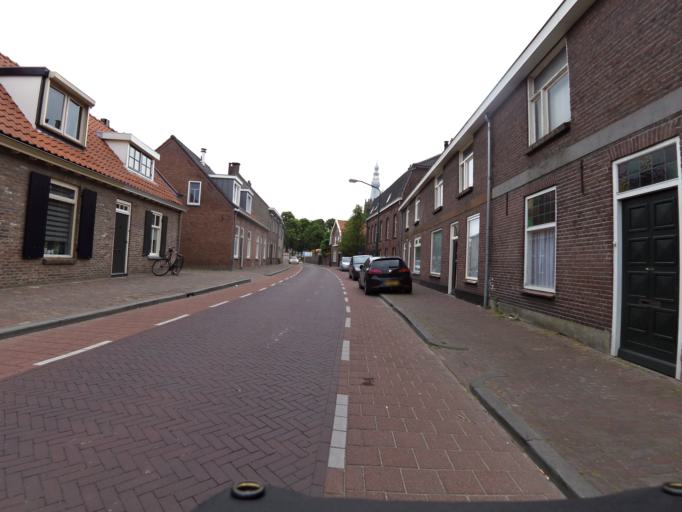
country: NL
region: North Brabant
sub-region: Gemeente Hilvarenbeek
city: Hilvarenbeek
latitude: 51.4860
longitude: 5.1334
